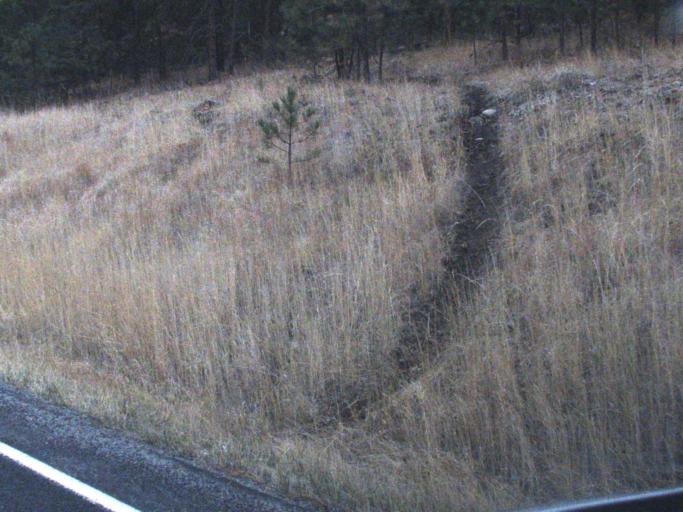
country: US
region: Washington
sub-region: Lincoln County
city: Davenport
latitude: 48.0013
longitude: -118.2759
